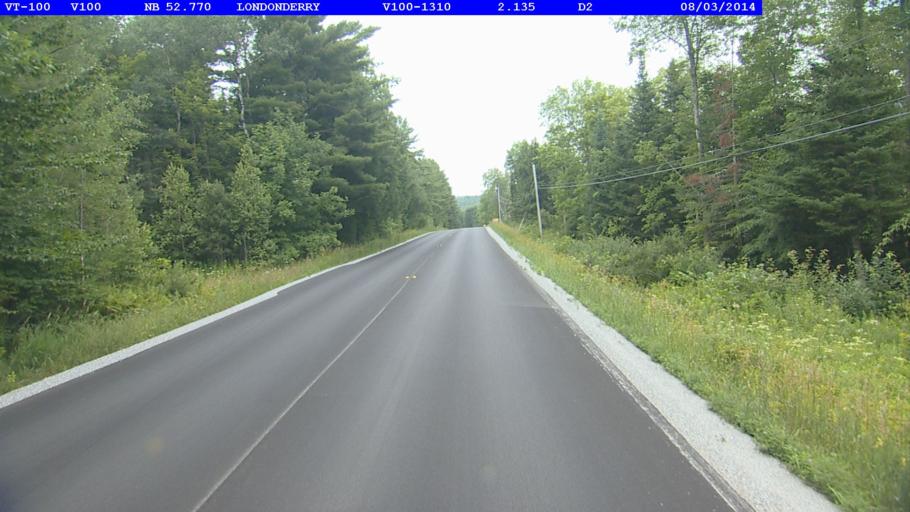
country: US
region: Vermont
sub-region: Windsor County
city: Chester
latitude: 43.1816
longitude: -72.8170
